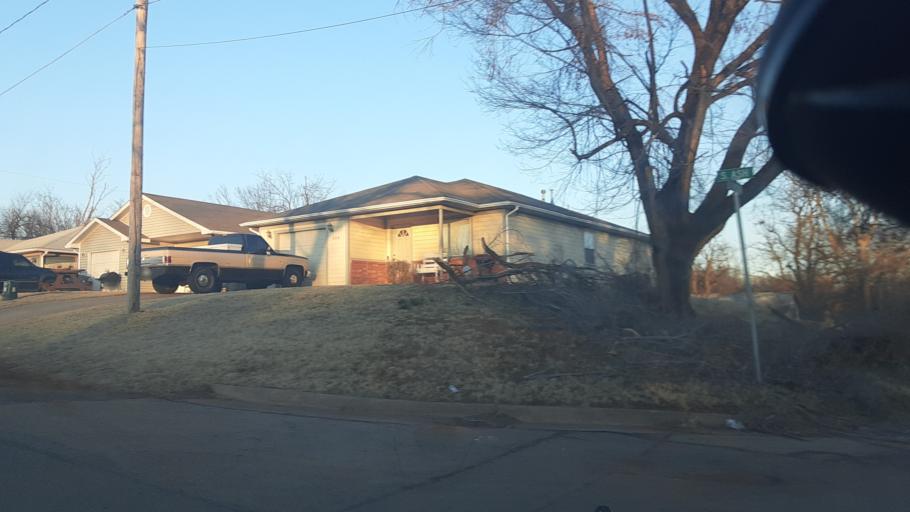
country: US
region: Oklahoma
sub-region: Logan County
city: Guthrie
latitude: 35.8718
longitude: -97.4215
